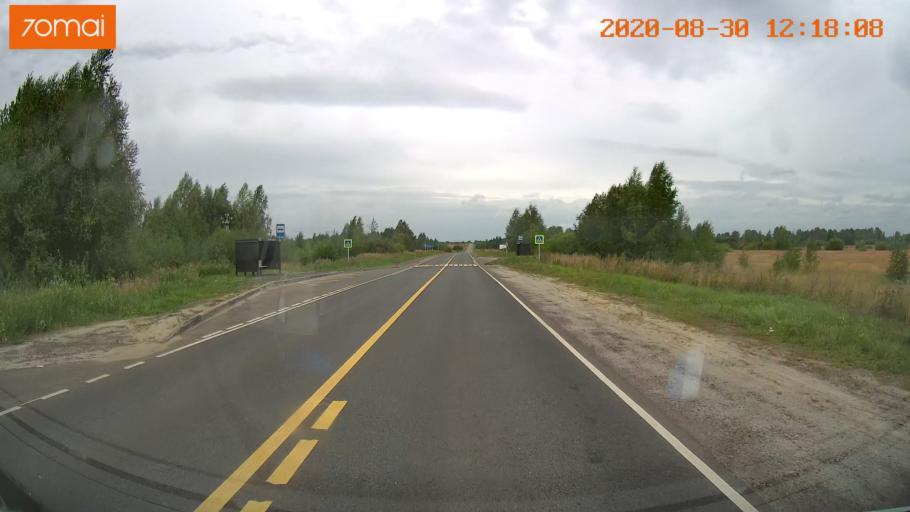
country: RU
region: Ivanovo
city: Yur'yevets
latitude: 57.3234
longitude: 42.9596
